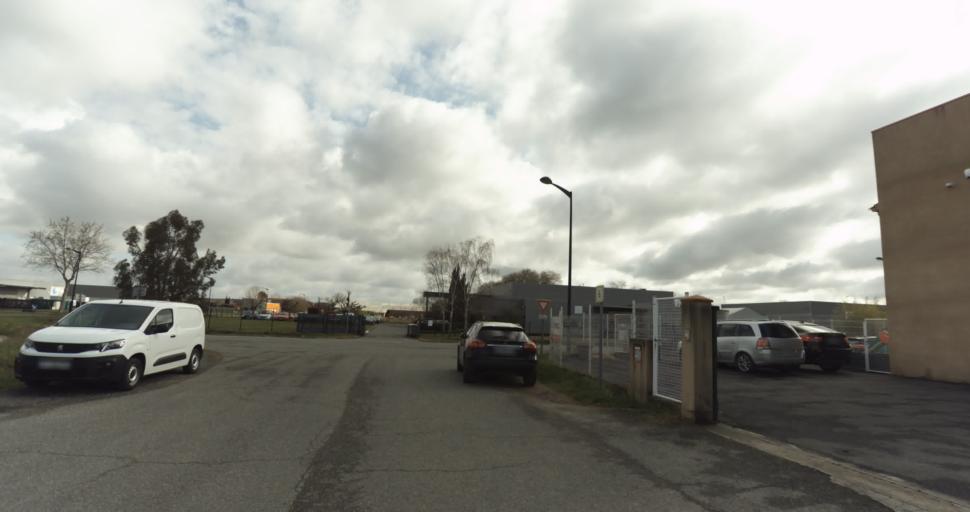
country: FR
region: Midi-Pyrenees
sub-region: Departement de la Haute-Garonne
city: Miremont
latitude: 43.3660
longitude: 1.4463
